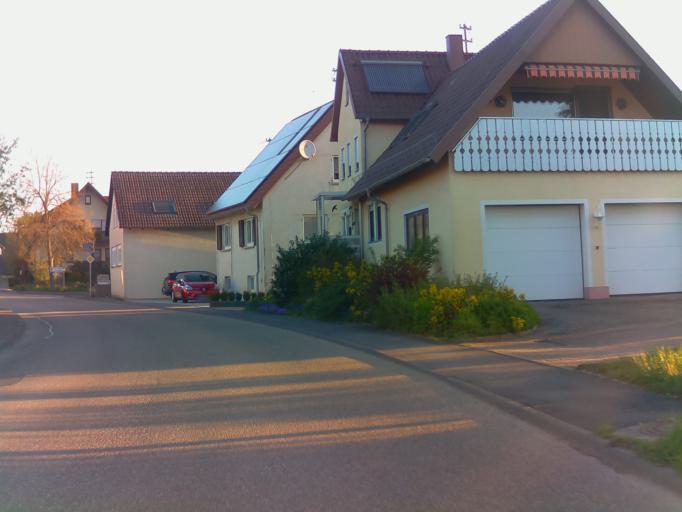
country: DE
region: Baden-Wuerttemberg
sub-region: Regierungsbezirk Stuttgart
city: Pfedelbach
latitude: 49.1762
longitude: 9.5303
